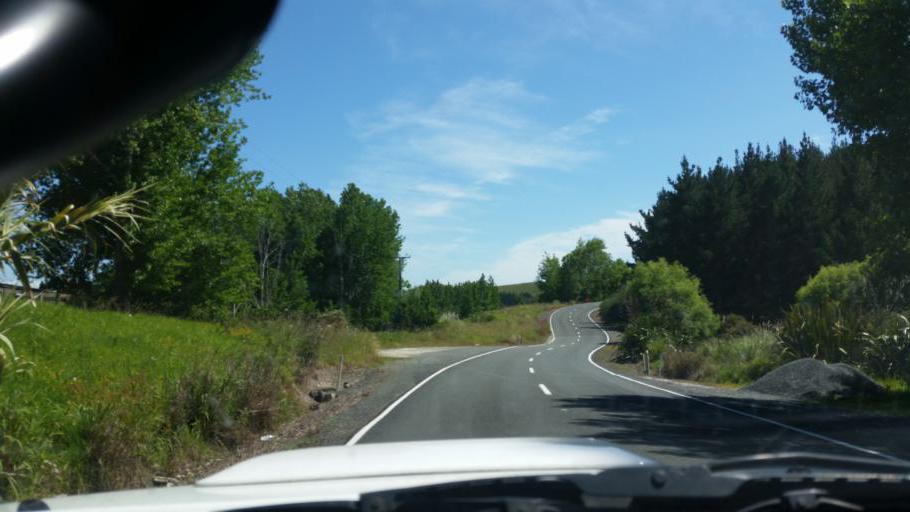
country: NZ
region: Auckland
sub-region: Auckland
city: Wellsford
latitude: -36.2096
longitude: 174.3918
